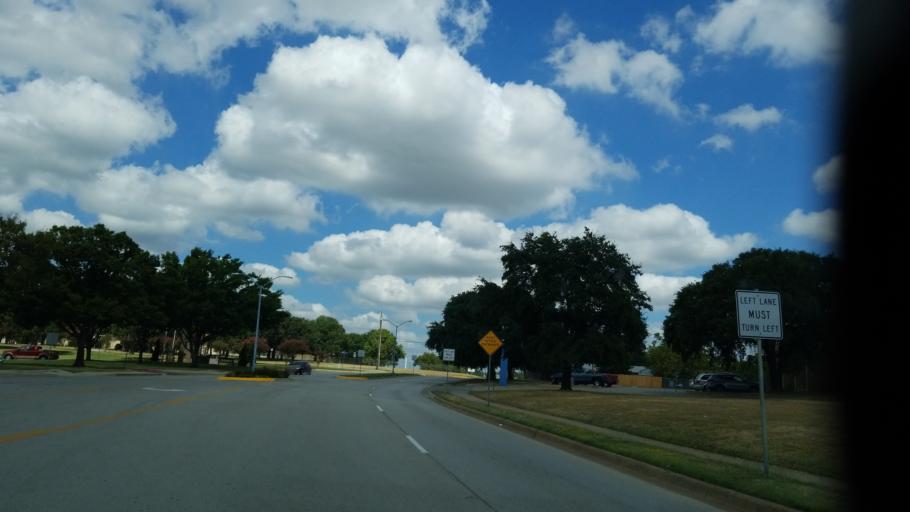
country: US
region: Texas
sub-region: Tarrant County
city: Euless
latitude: 32.8399
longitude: -97.0915
